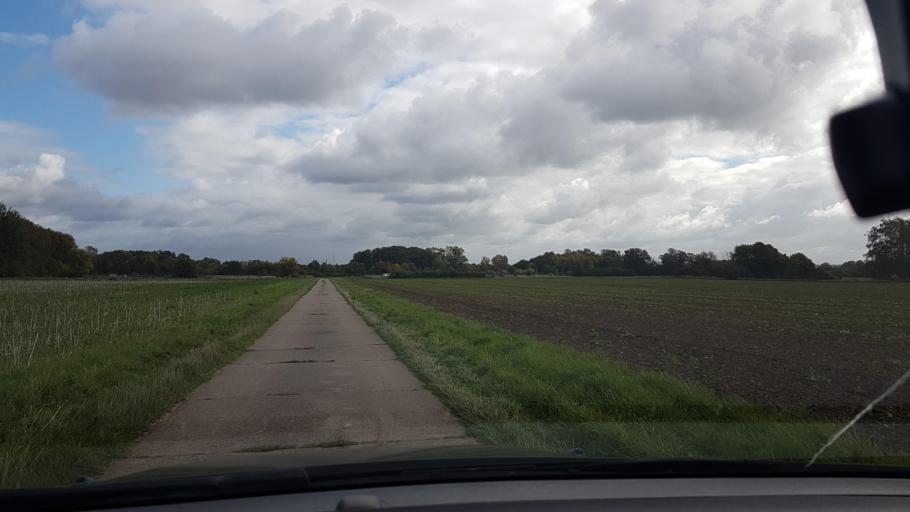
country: DE
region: Lower Saxony
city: Ronnenberg
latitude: 52.3425
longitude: 9.6359
